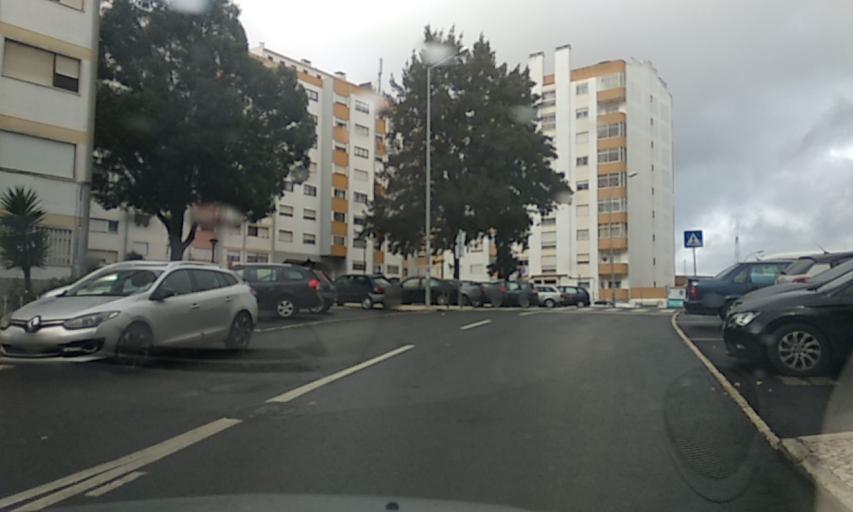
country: PT
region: Lisbon
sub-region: Sintra
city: Cacem
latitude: 38.7547
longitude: -9.2866
